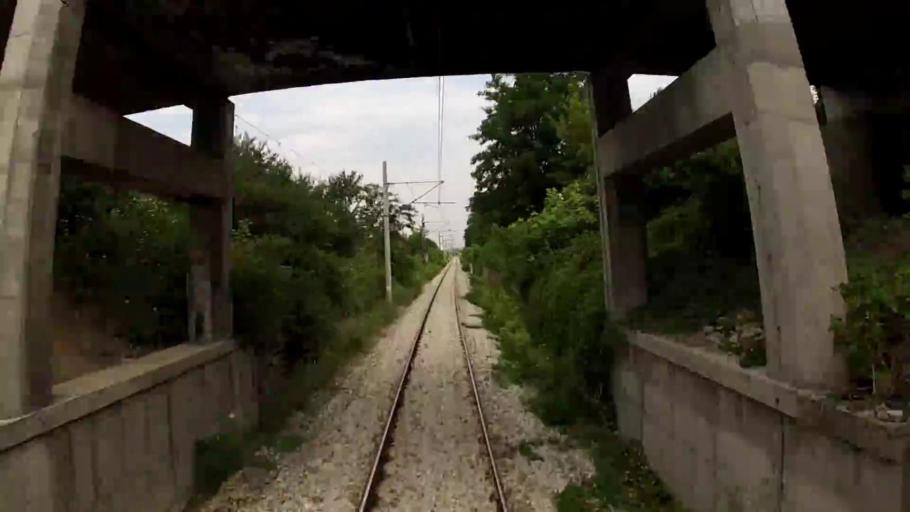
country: BG
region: Blagoevgrad
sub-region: Obshtina Blagoevgrad
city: Blagoevgrad
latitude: 41.9785
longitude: 23.0896
